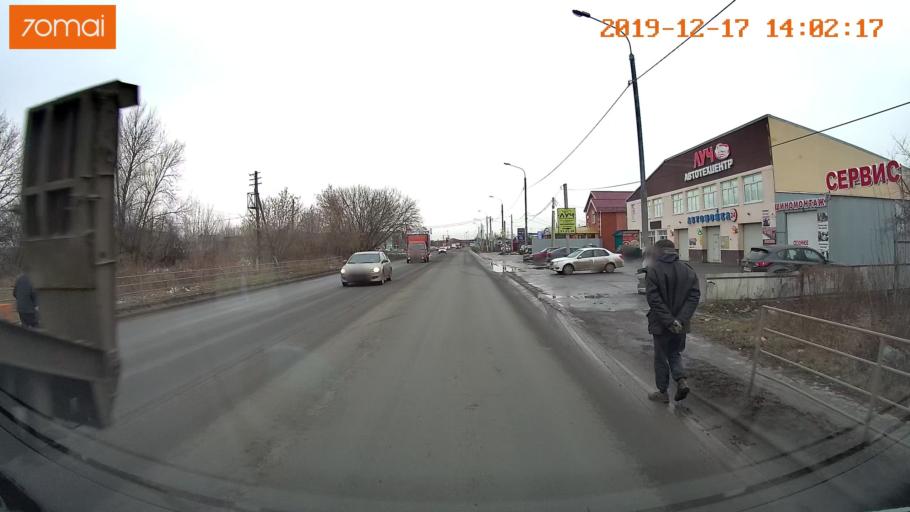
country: RU
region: Rjazan
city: Ryazan'
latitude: 54.6151
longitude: 39.6487
